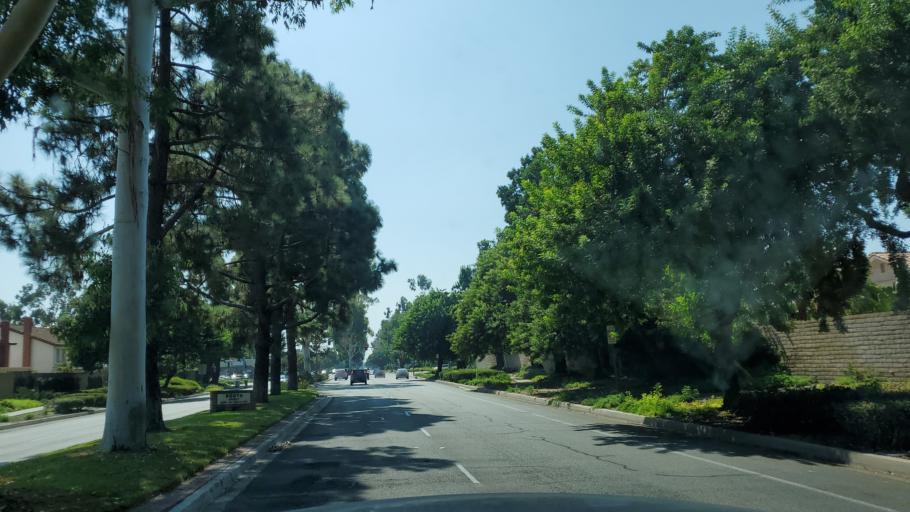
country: US
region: California
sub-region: Los Angeles County
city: Cerritos
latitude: 33.8600
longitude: -118.0637
